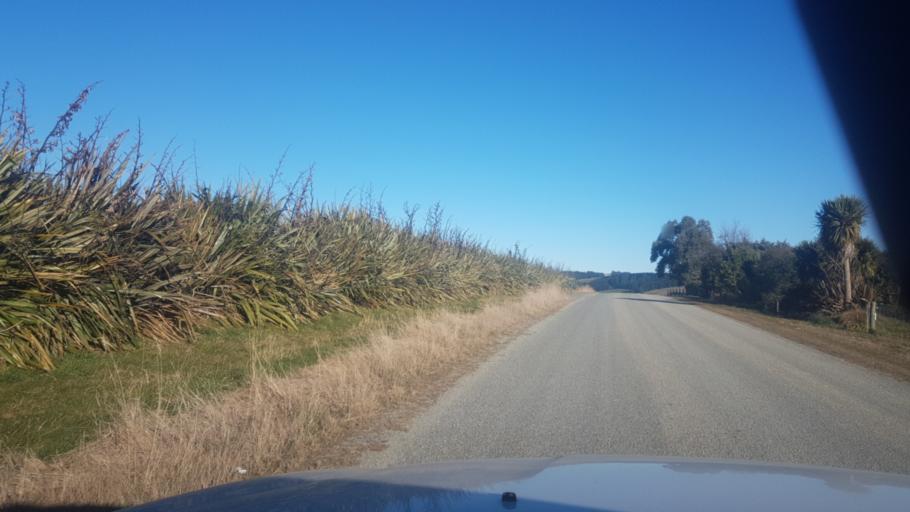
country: NZ
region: Canterbury
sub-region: Timaru District
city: Pleasant Point
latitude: -44.3602
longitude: 171.0697
